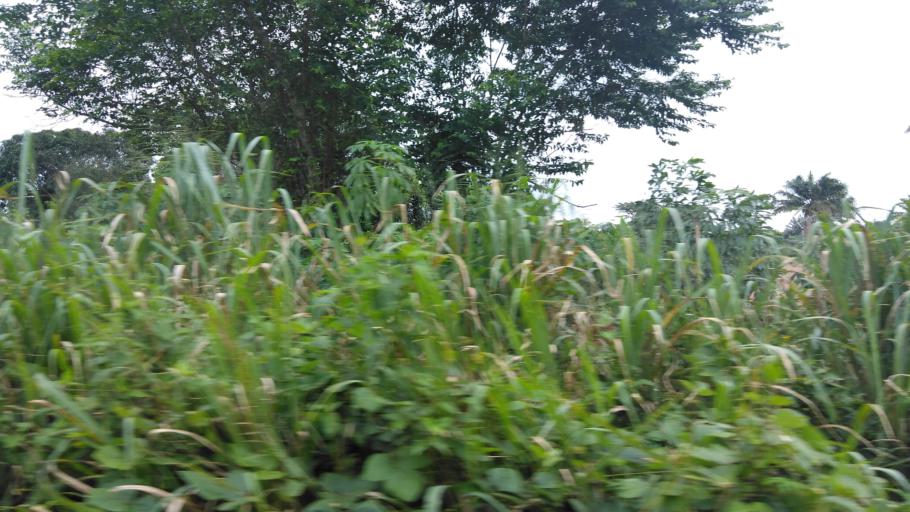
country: NG
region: Ogun
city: Abigi
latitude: 6.5926
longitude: 4.4989
